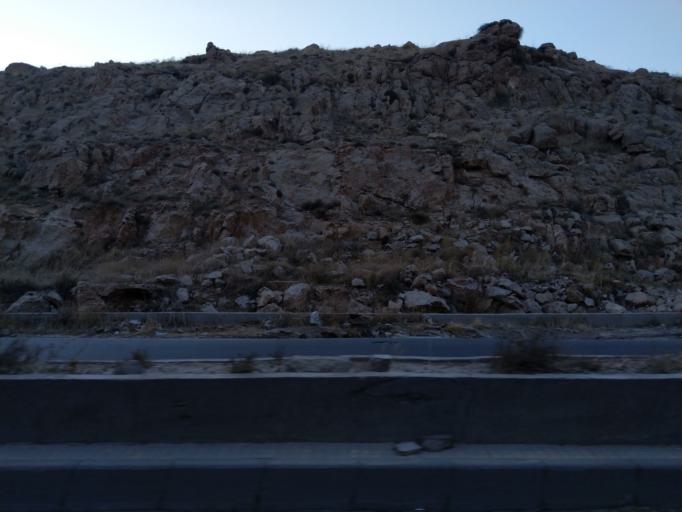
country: SY
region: Rif-dimashq
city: At Tall
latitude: 33.5694
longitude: 36.3063
